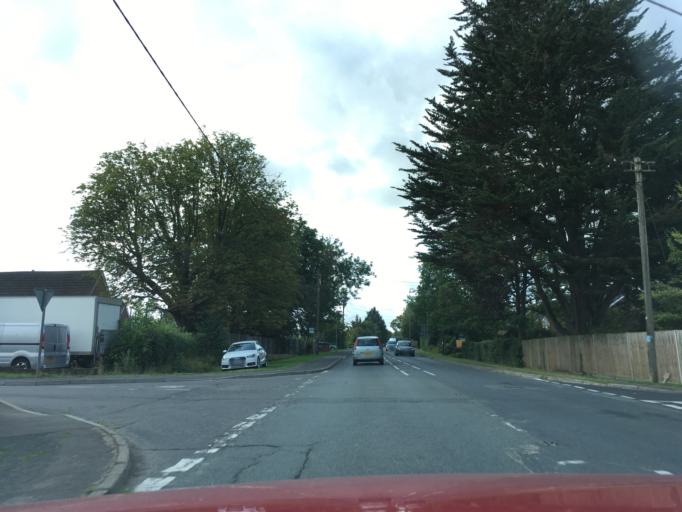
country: GB
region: England
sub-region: Hampshire
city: Bishops Waltham
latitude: 50.9390
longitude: -1.2015
